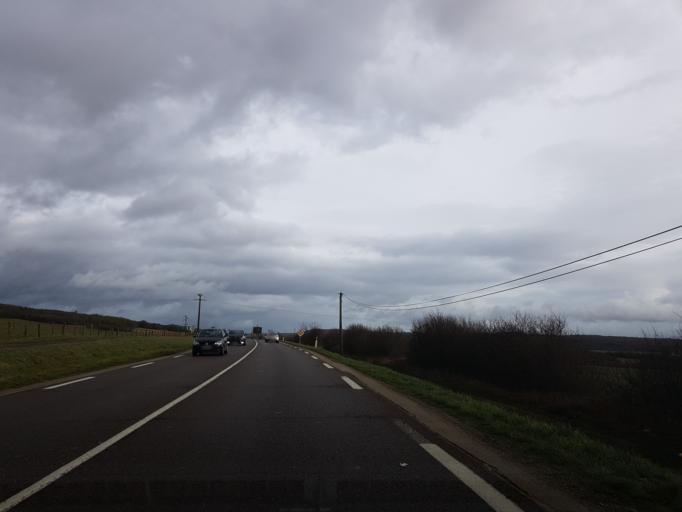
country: FR
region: Franche-Comte
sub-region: Departement de la Haute-Saone
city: Frotey-les-Vesoul
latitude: 47.6233
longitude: 6.1934
